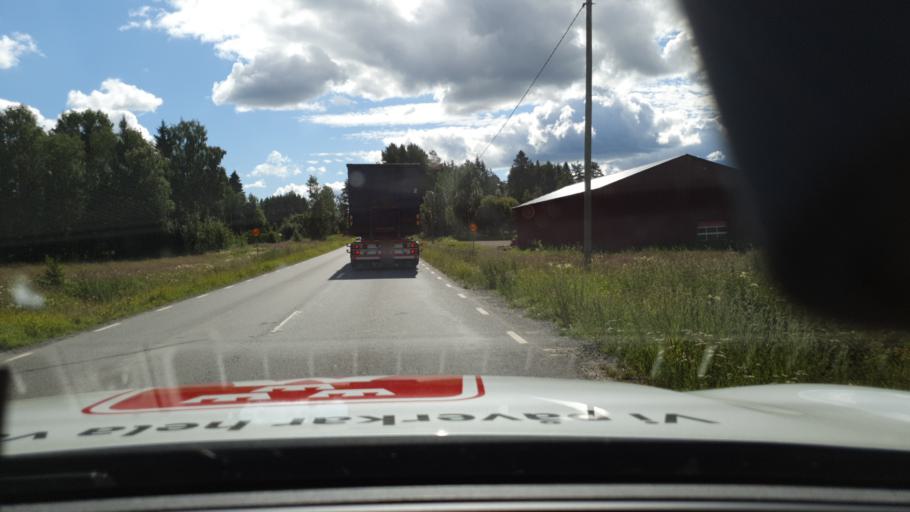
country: SE
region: Norrbotten
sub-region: Lulea Kommun
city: Gammelstad
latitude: 65.7932
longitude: 22.0747
